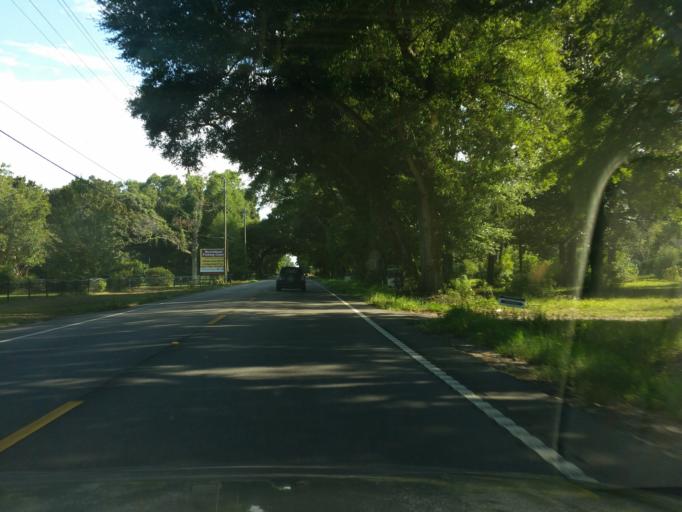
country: US
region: Alabama
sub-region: Mobile County
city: Theodore
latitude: 30.4761
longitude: -88.1135
